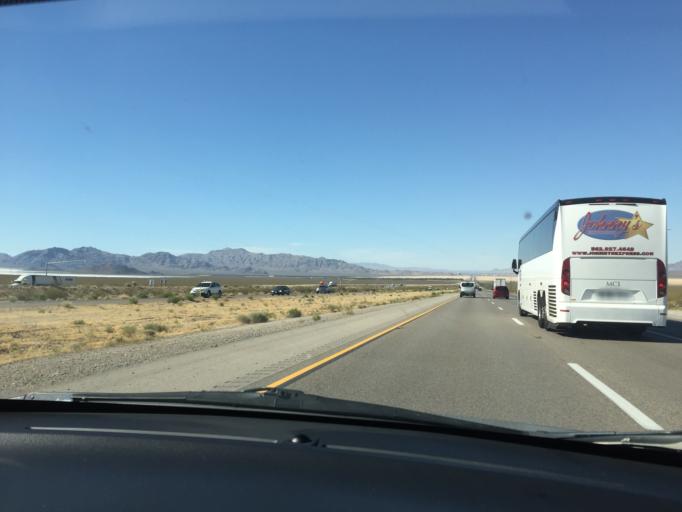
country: US
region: Nevada
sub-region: Clark County
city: Sandy Valley
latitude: 35.5051
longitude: -115.4349
